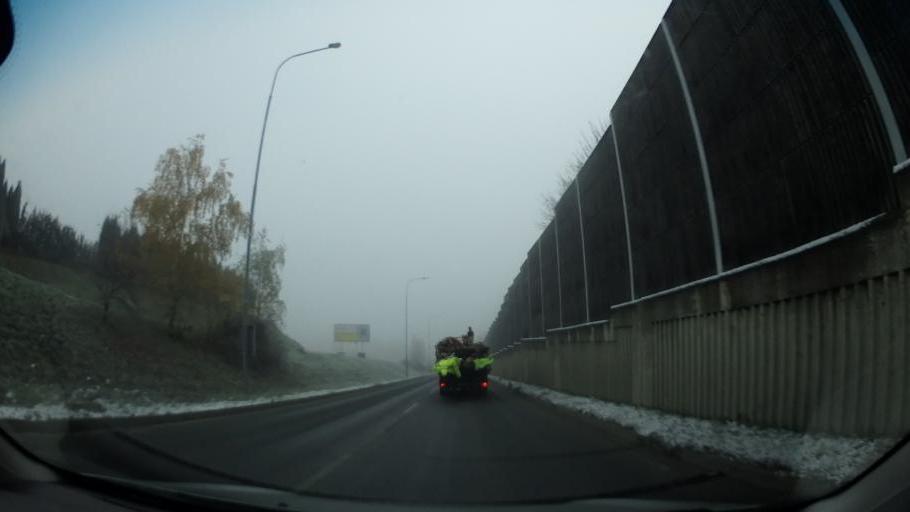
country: CZ
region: Vysocina
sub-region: Okres Trebic
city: Trebic
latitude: 49.2223
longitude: 15.8961
